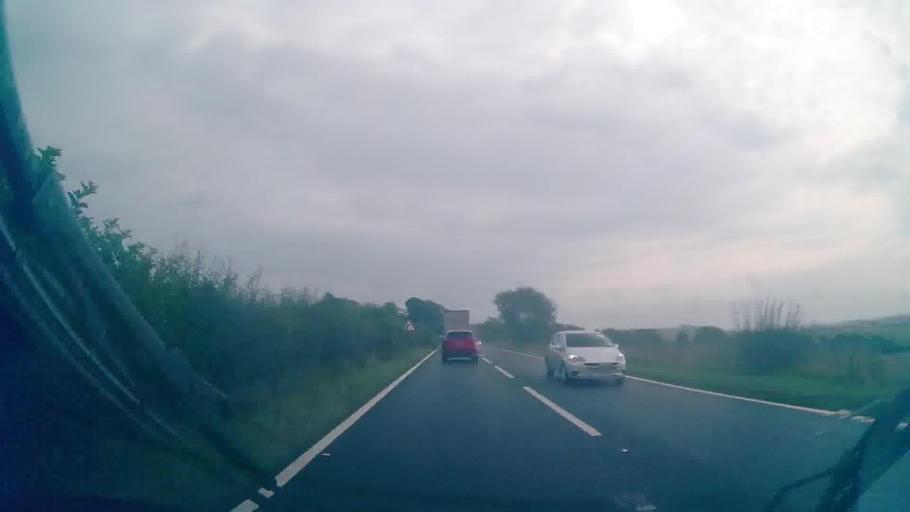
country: GB
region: Scotland
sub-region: Dumfries and Galloway
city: Lochmaben
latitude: 55.0539
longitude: -3.4673
